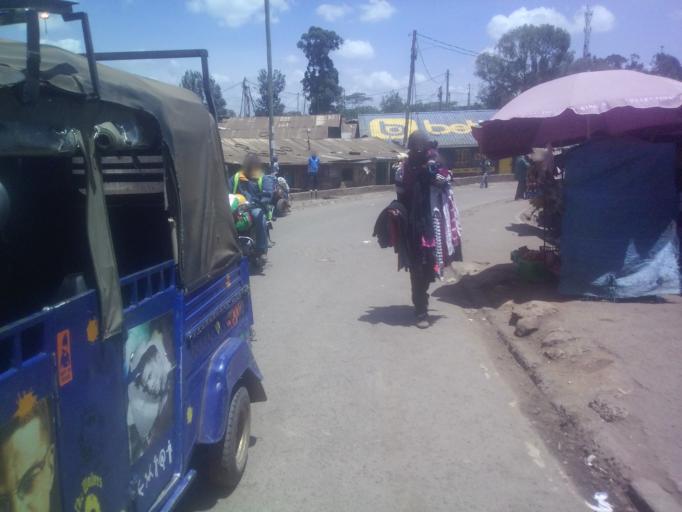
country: KE
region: Nairobi Area
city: Nairobi
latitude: -1.3074
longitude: 36.7862
